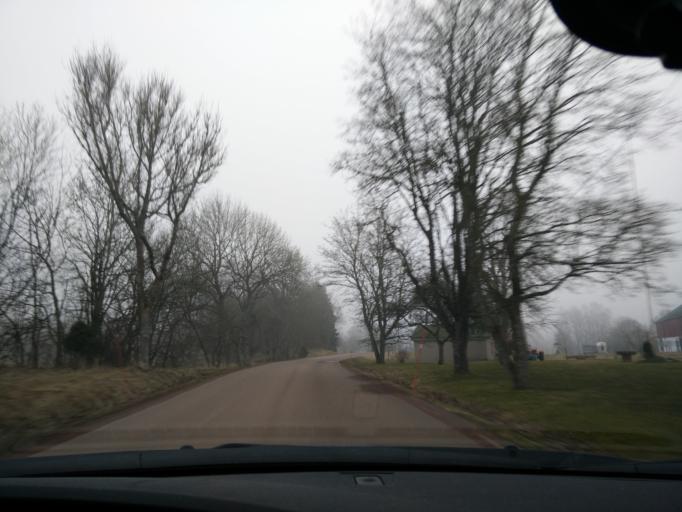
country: AX
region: Mariehamns stad
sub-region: Mariehamn
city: Mariehamn
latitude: 60.1048
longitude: 19.9001
